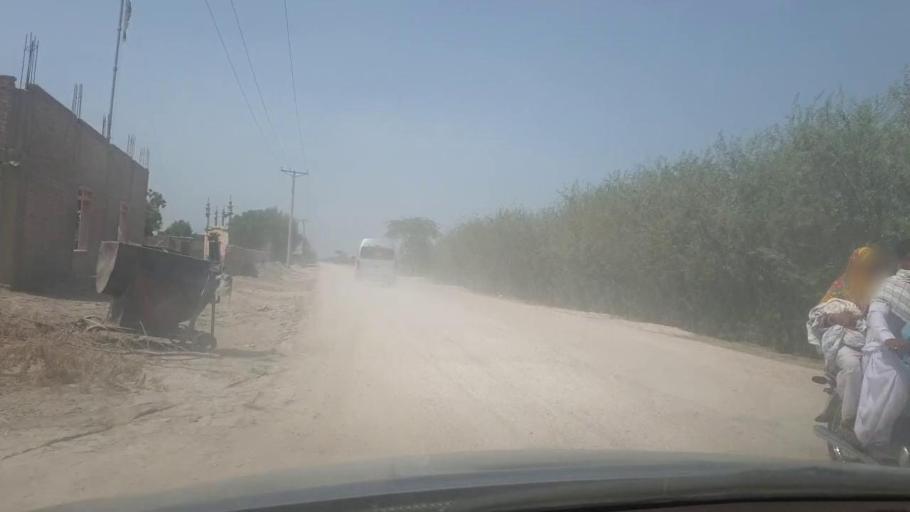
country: PK
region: Sindh
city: Ranipur
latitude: 27.2745
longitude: 68.5972
